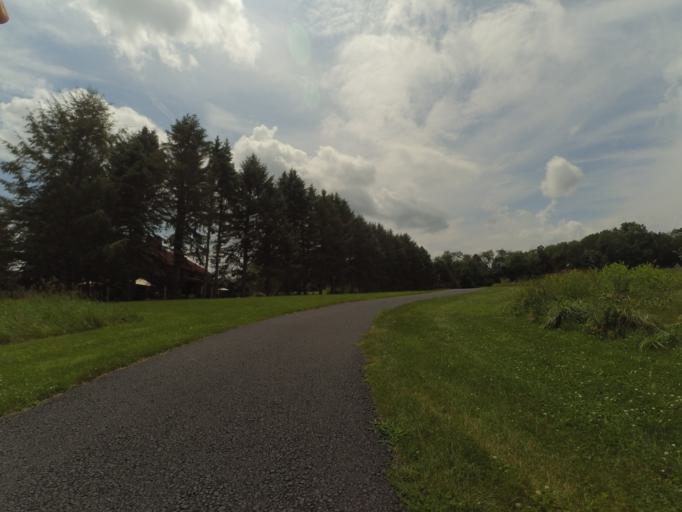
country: US
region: Pennsylvania
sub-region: Centre County
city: Park Forest Village
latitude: 40.7975
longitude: -77.8932
